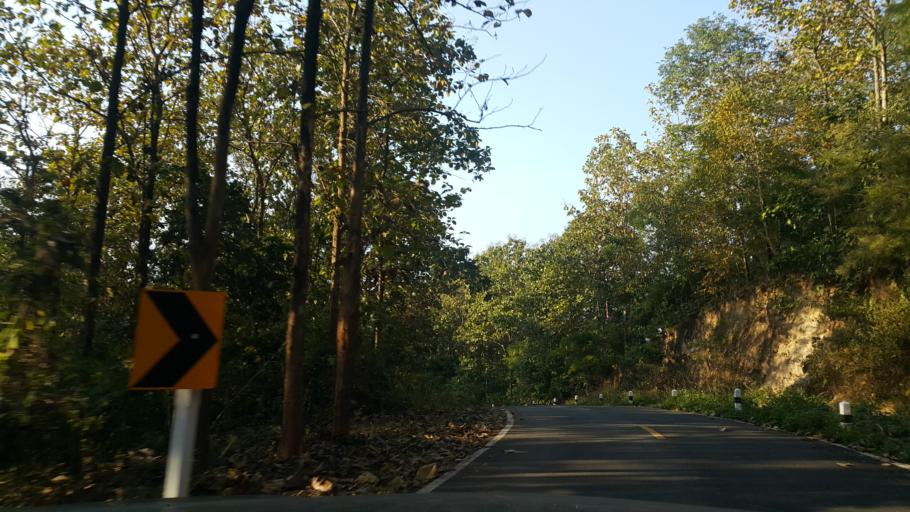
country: TH
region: Lampang
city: Hang Chat
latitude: 18.3510
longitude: 99.2494
